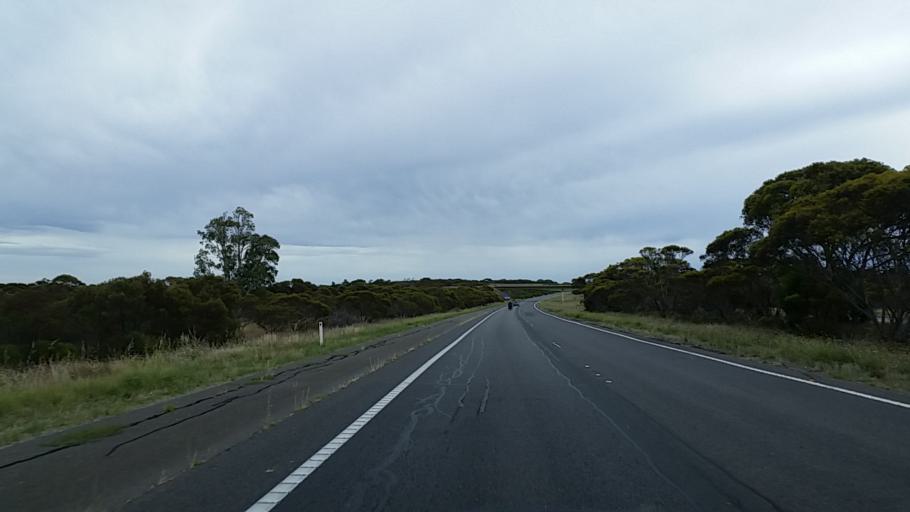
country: AU
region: South Australia
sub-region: Murray Bridge
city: Murray Bridge
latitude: -35.1524
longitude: 139.1974
